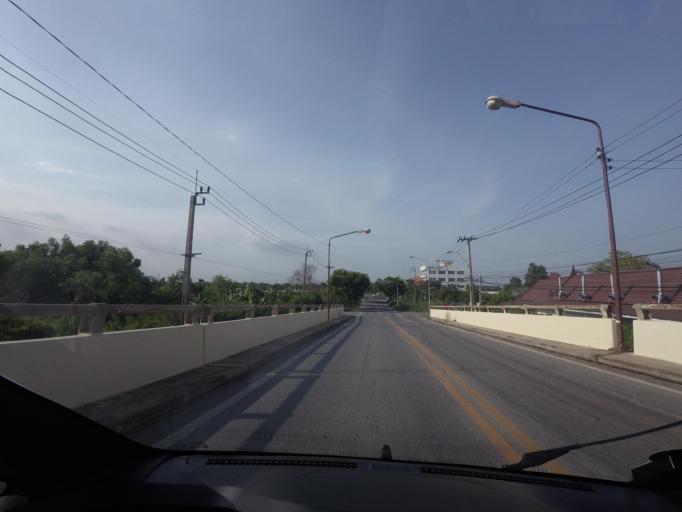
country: TH
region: Samut Prakan
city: Ban Khlong Bang Sao Thong
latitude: 13.7010
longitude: 100.8528
